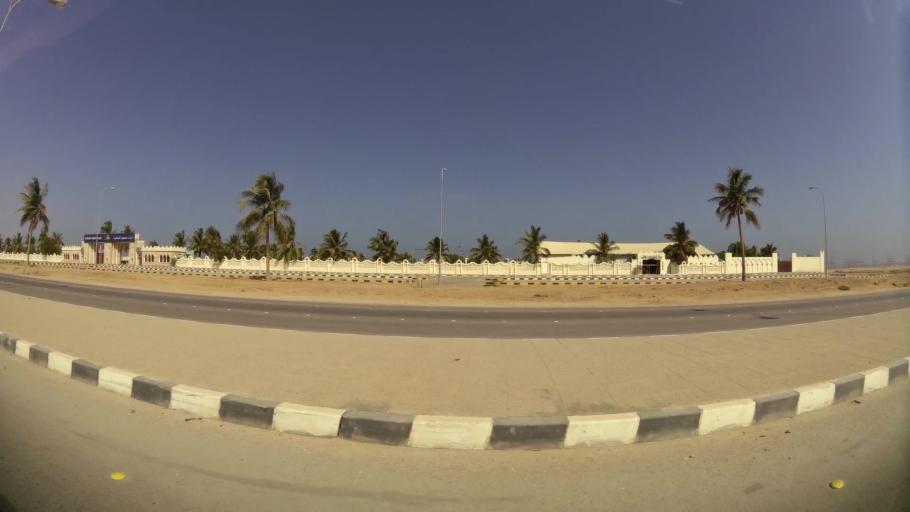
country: OM
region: Zufar
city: Salalah
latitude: 16.9895
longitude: 54.0241
